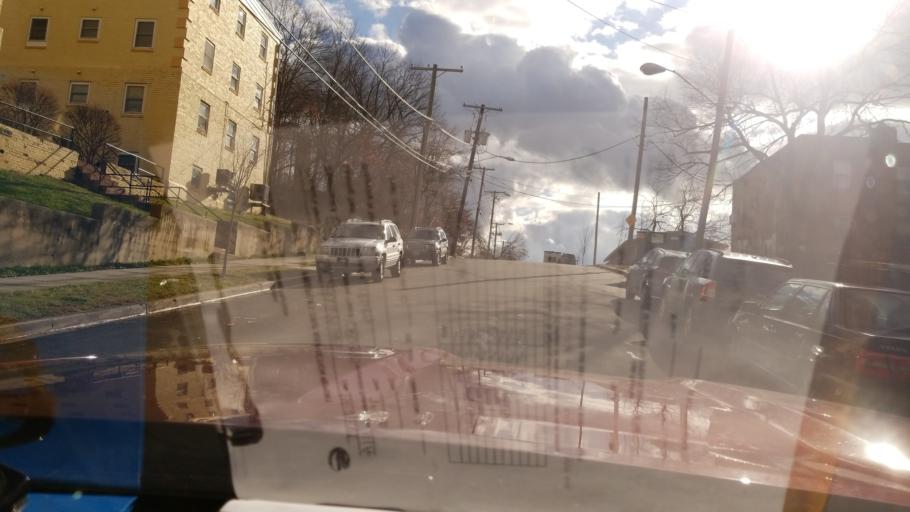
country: US
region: Maryland
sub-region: Prince George's County
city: Glassmanor
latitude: 38.8293
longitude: -77.0021
